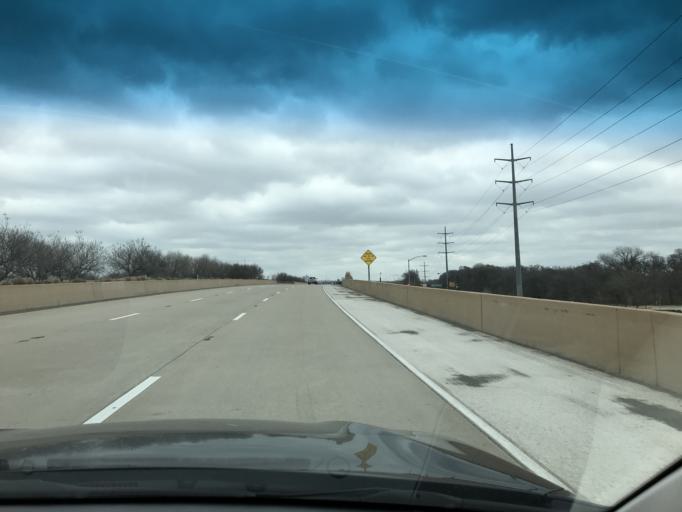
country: US
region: Texas
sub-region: Tarrant County
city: Westworth
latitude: 32.7118
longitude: -97.3999
